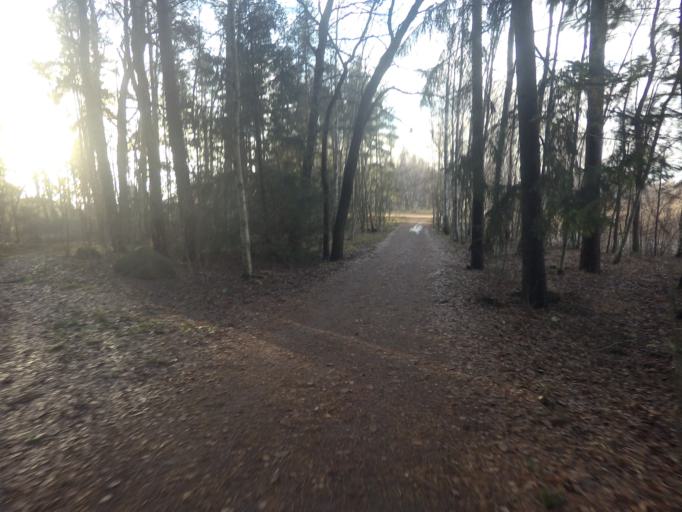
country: FI
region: Uusimaa
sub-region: Helsinki
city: Teekkarikylae
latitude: 60.1910
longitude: 24.8308
